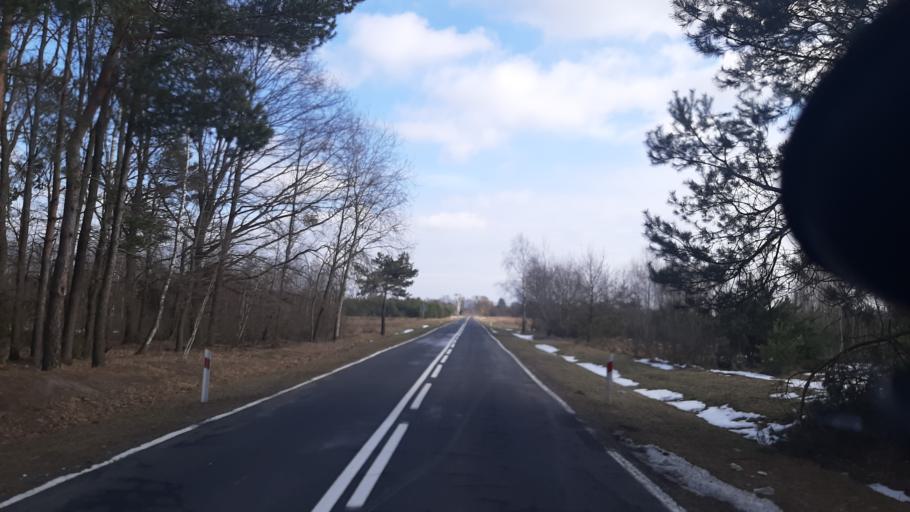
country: PL
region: Lublin Voivodeship
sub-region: Powiat wlodawski
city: Urszulin
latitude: 51.4990
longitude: 23.2017
